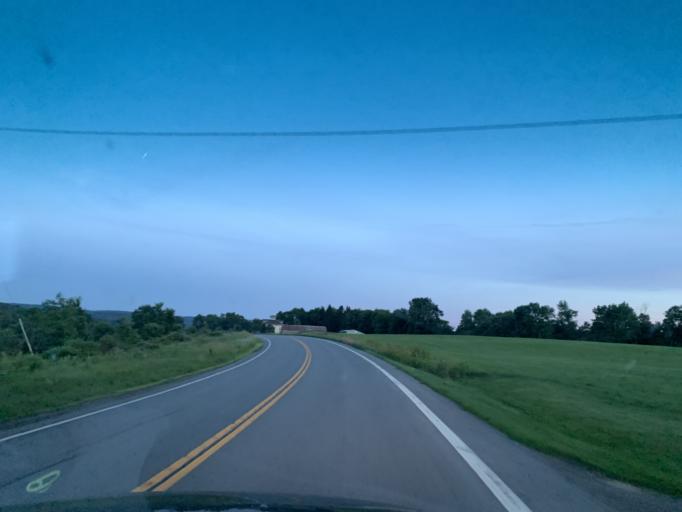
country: US
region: New York
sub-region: Chenango County
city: New Berlin
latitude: 42.6497
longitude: -75.3319
